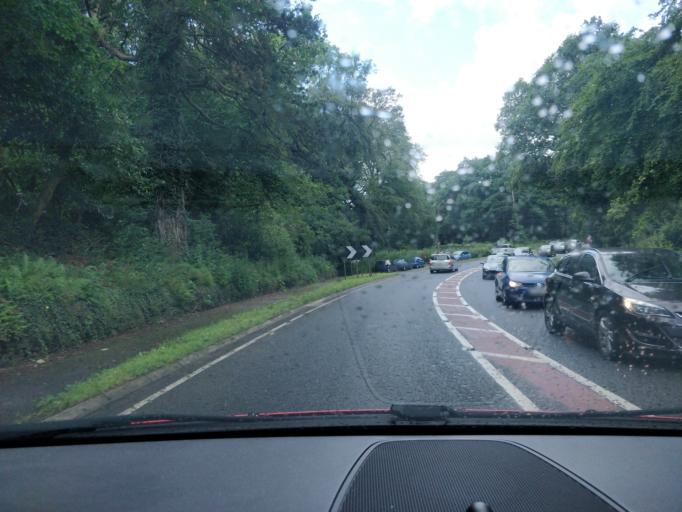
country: GB
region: Wales
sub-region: Conwy
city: Betws-y-Coed
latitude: 53.0976
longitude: -3.7885
